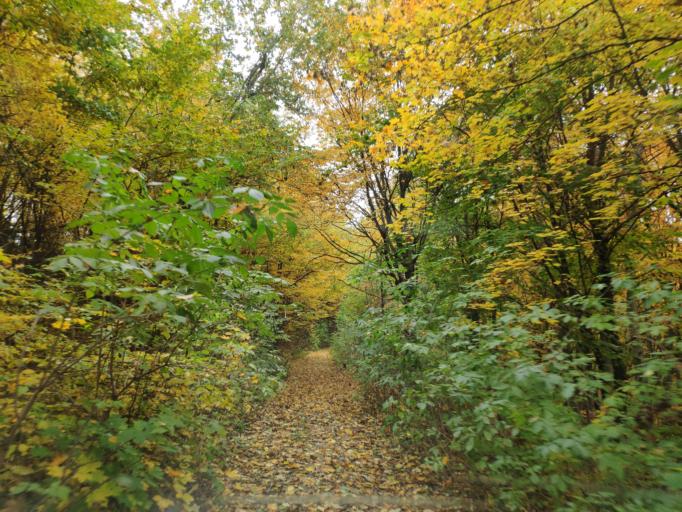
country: SK
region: Kosicky
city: Moldava nad Bodvou
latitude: 48.7232
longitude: 21.1021
